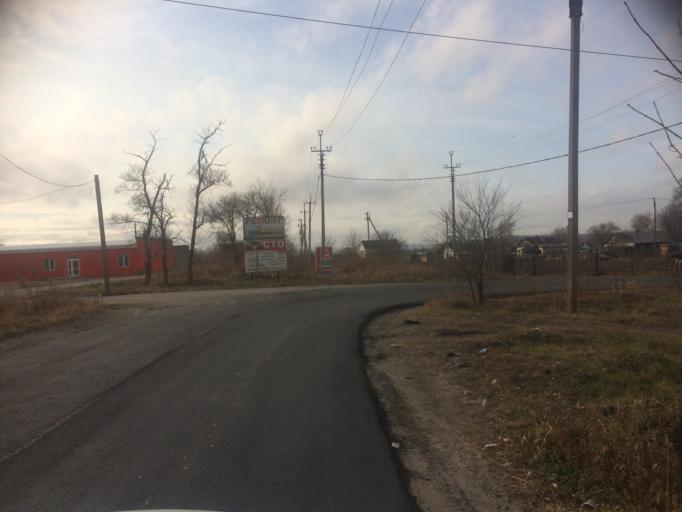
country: RU
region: Primorskiy
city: Mikhaylovka
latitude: 43.9370
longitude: 132.0228
